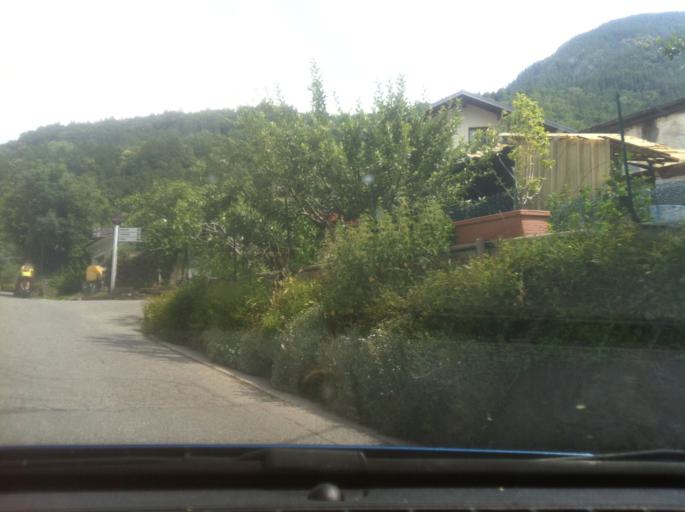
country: IT
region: Aosta Valley
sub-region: Valle d'Aosta
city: Saint Marcel
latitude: 45.7287
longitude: 7.4451
